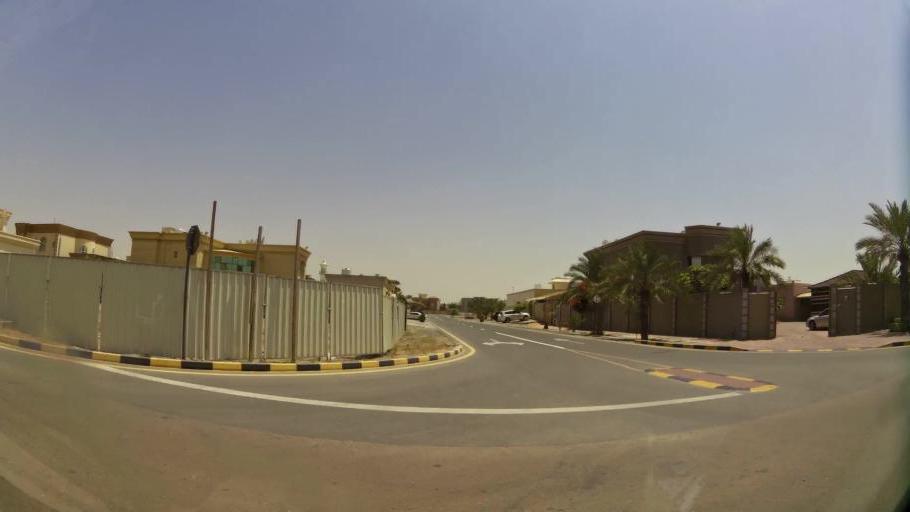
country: AE
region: Ajman
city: Ajman
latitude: 25.4269
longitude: 55.5175
